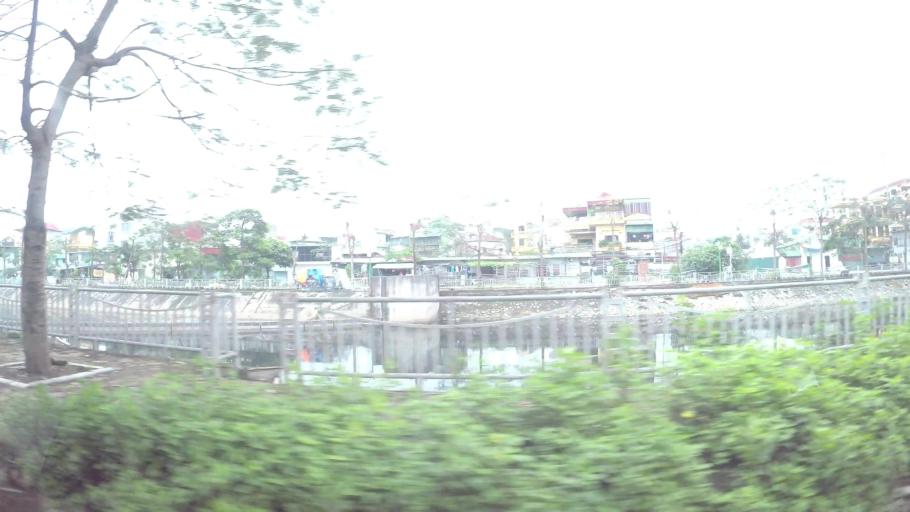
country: VN
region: Ha Noi
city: Van Dien
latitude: 20.9725
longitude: 105.8528
